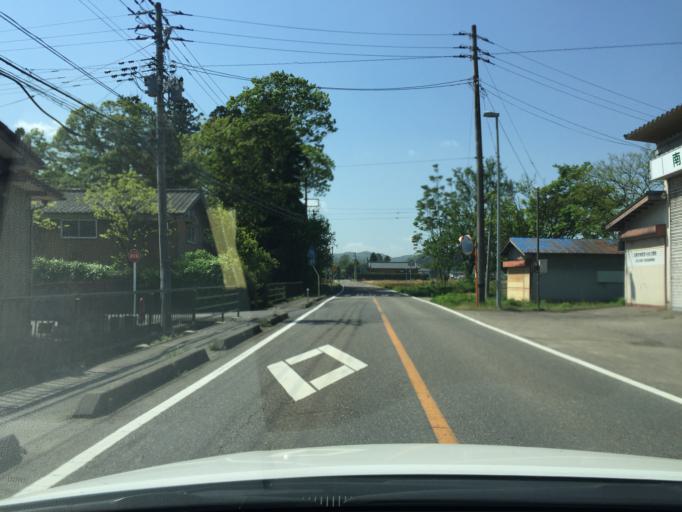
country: JP
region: Niigata
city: Muramatsu
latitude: 37.6769
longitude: 139.1497
